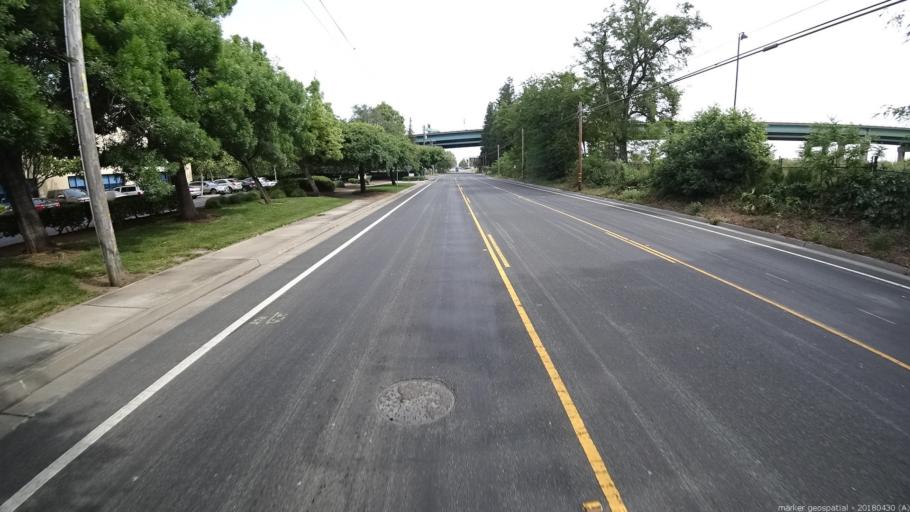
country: US
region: California
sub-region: Yolo County
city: West Sacramento
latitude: 38.5724
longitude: -121.5198
